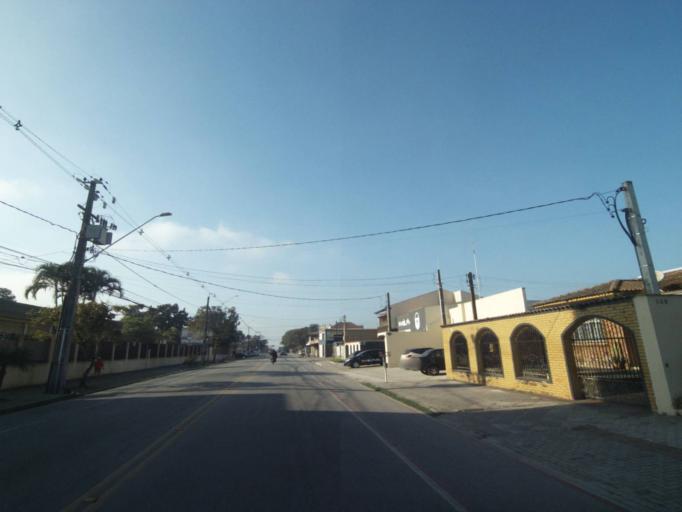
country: BR
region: Parana
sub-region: Paranagua
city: Paranagua
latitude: -25.5231
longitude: -48.5153
